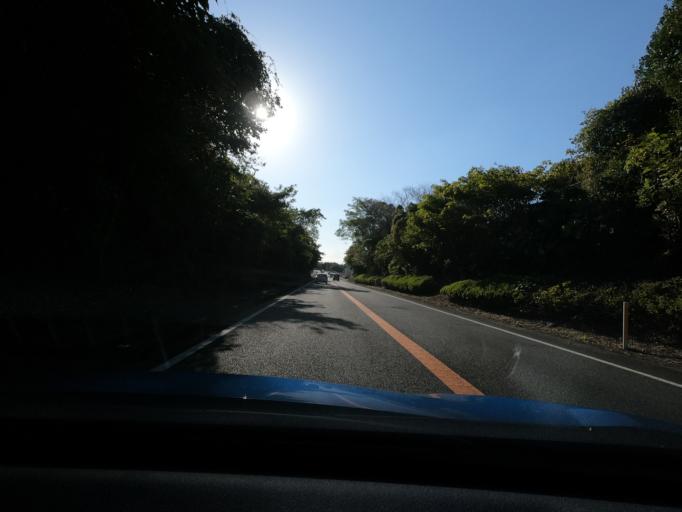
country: JP
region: Kagoshima
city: Izumi
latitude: 32.1314
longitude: 130.3482
